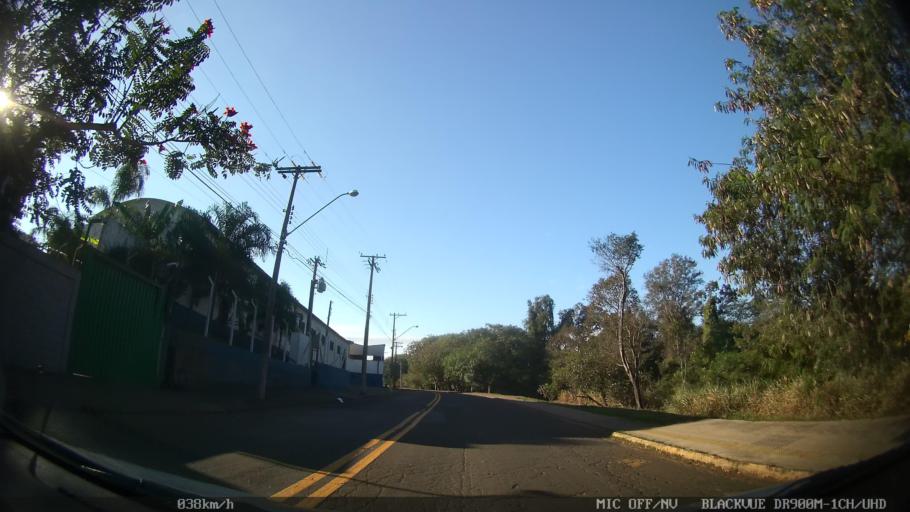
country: BR
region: Sao Paulo
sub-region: Piracicaba
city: Piracicaba
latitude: -22.6773
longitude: -47.6321
